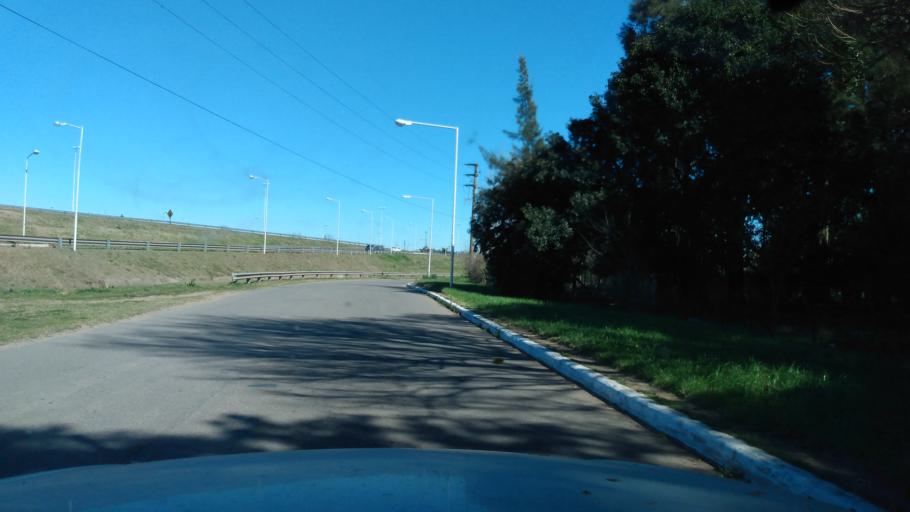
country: AR
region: Buenos Aires
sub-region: Partido de Lujan
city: Lujan
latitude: -34.5553
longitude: -59.0991
